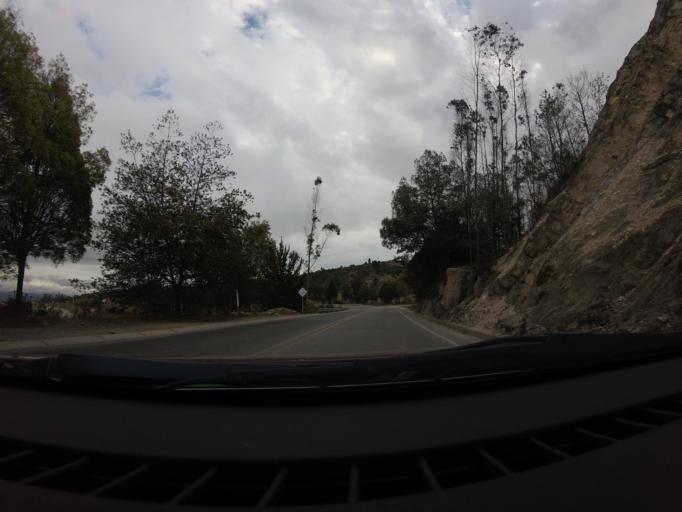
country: CO
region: Boyaca
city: Cucaita
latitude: 5.5625
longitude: -73.4139
